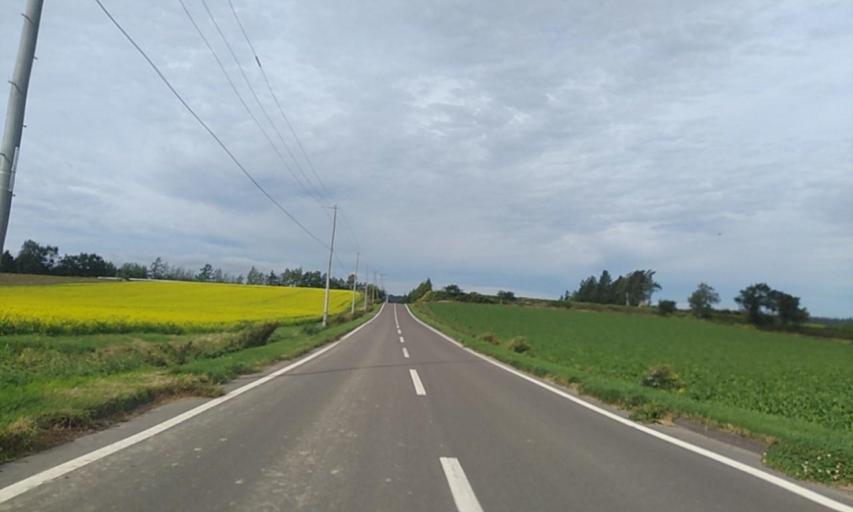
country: JP
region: Hokkaido
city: Abashiri
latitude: 43.7959
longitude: 144.5640
